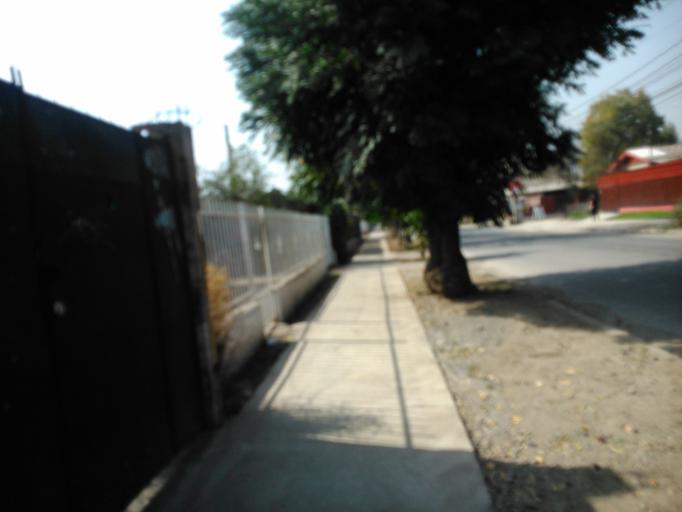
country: CL
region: Santiago Metropolitan
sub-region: Provincia de Cordillera
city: Puente Alto
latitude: -33.5562
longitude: -70.5840
